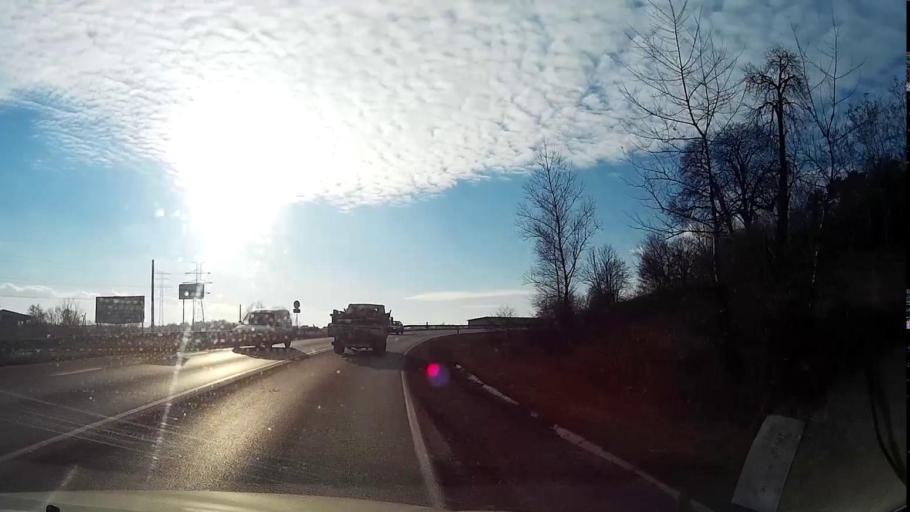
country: PL
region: Lesser Poland Voivodeship
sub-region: Powiat krakowski
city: Kryspinow
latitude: 50.0413
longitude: 19.8034
